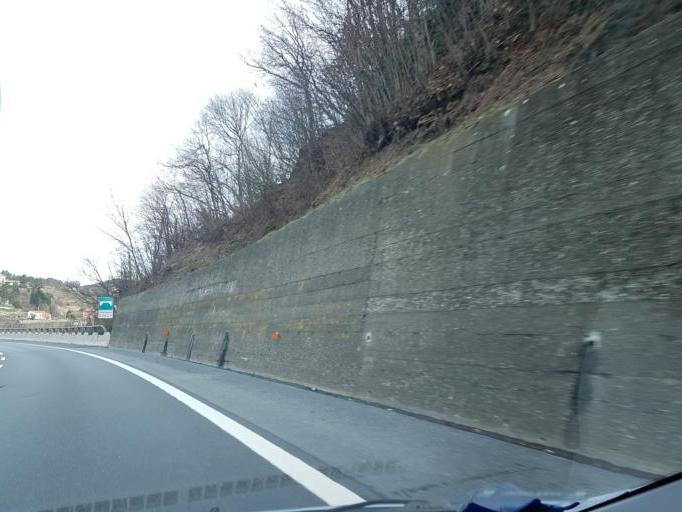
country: IT
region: Liguria
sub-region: Provincia di Genova
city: Serra Ricco
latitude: 44.5373
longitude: 8.9431
